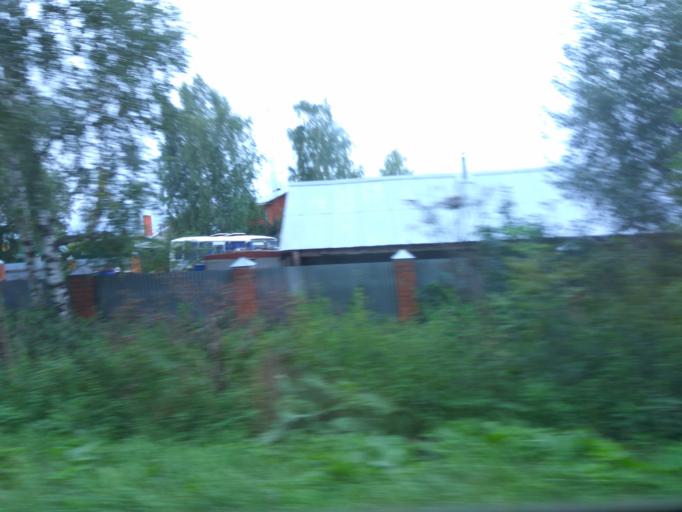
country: RU
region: Moskovskaya
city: Malyshevo
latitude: 55.5341
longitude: 38.3296
